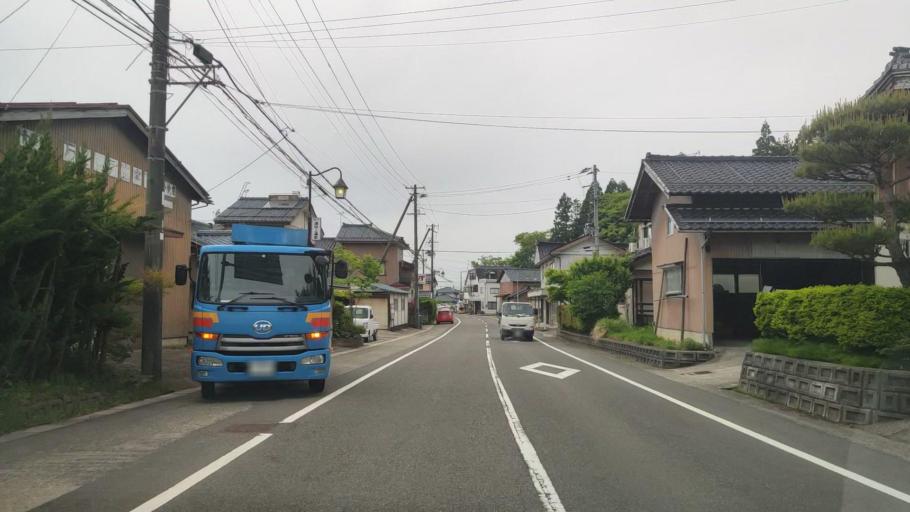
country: JP
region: Niigata
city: Kamo
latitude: 37.7123
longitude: 139.0753
